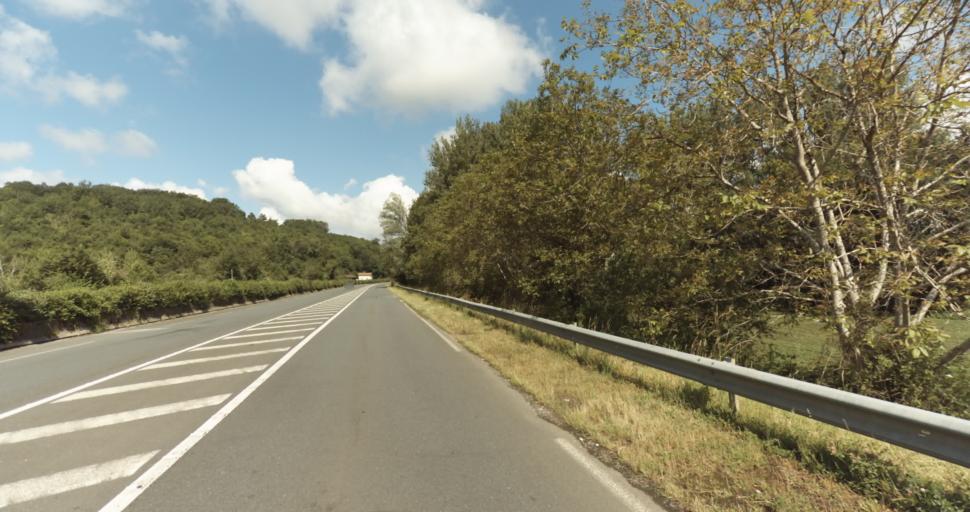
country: FR
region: Aquitaine
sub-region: Departement de la Dordogne
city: Belves
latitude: 44.8266
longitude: 0.9501
